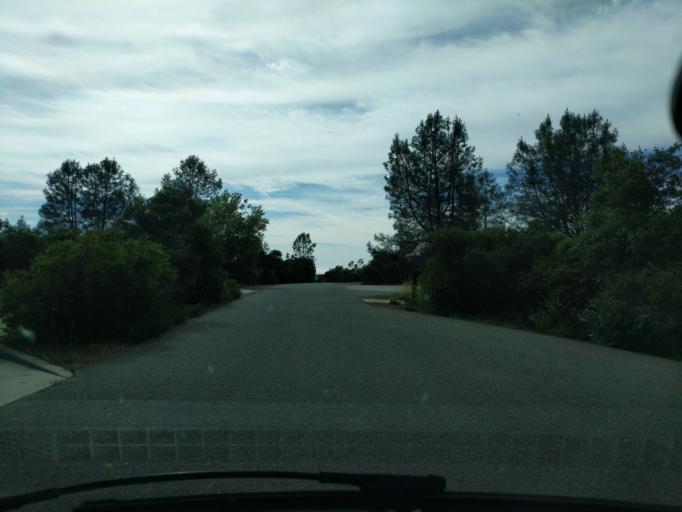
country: US
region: California
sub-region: Contra Costa County
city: Diablo
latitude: 37.8773
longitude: -121.9323
